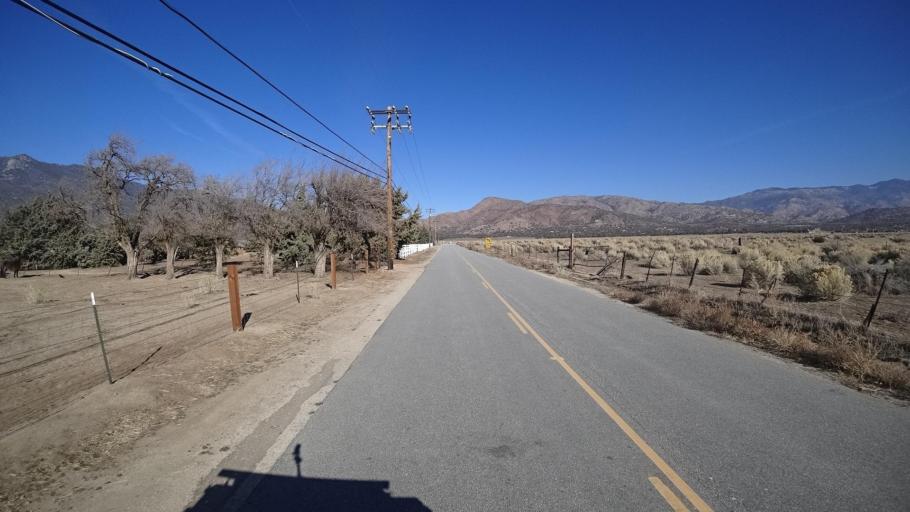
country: US
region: California
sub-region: Kern County
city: Bodfish
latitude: 35.4110
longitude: -118.5235
